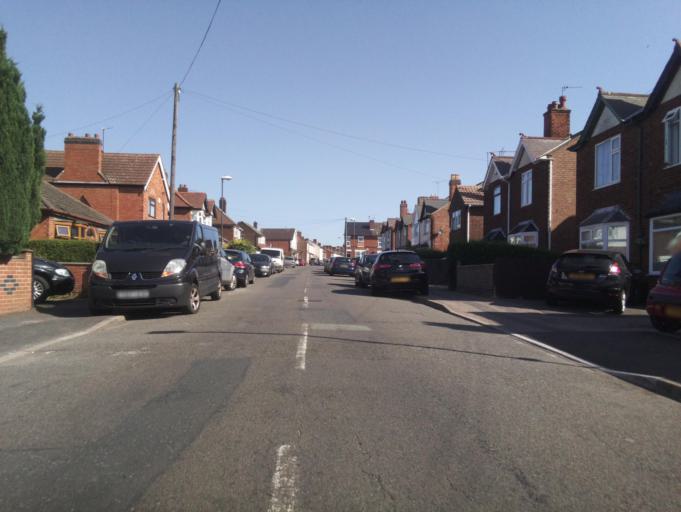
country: GB
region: England
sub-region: Derby
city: Derby
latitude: 52.9146
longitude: -1.4970
